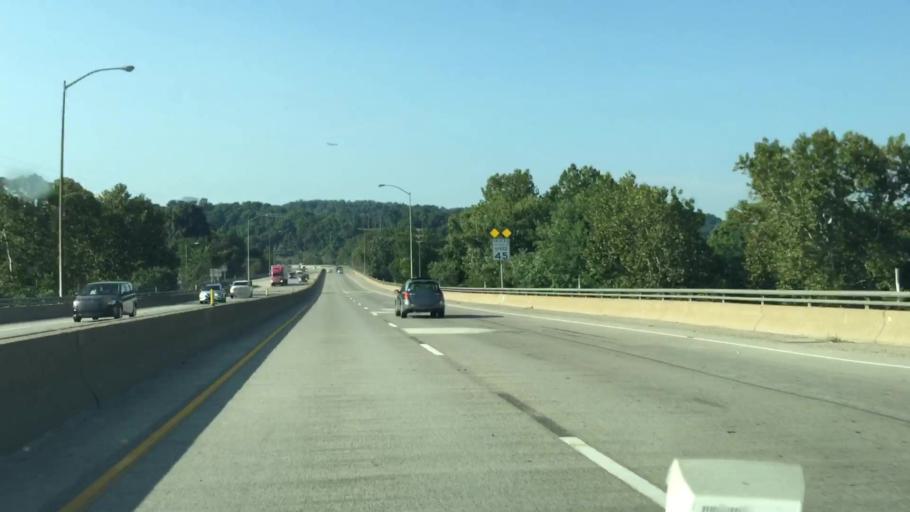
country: US
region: Pennsylvania
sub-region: Allegheny County
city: Coraopolis
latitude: 40.5099
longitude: -80.1365
